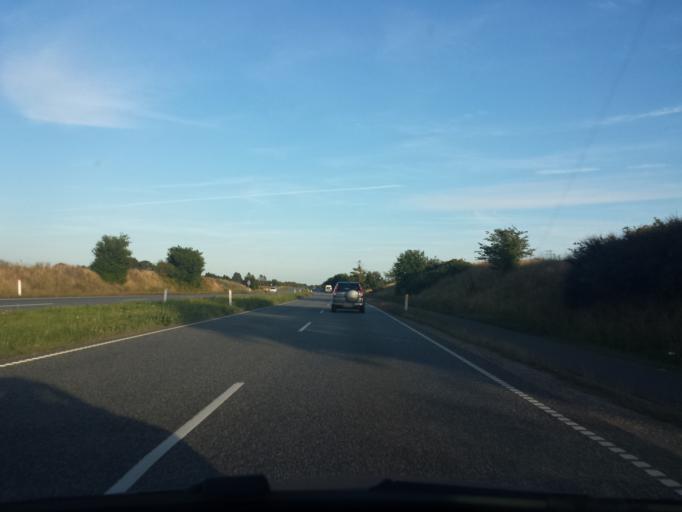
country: DK
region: Capital Region
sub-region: Egedal Kommune
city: Stenlose
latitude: 55.7646
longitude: 12.2132
